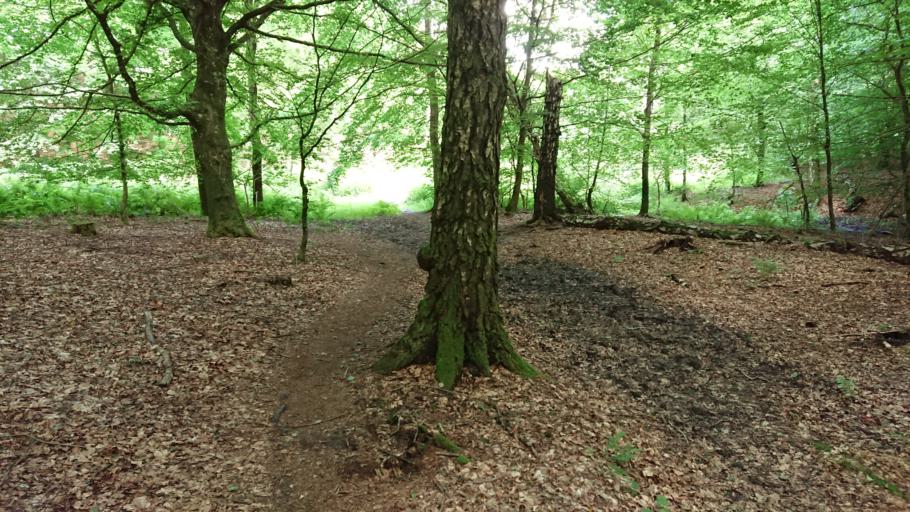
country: DK
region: North Denmark
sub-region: Hjorring Kommune
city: Sindal
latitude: 57.4494
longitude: 10.3330
